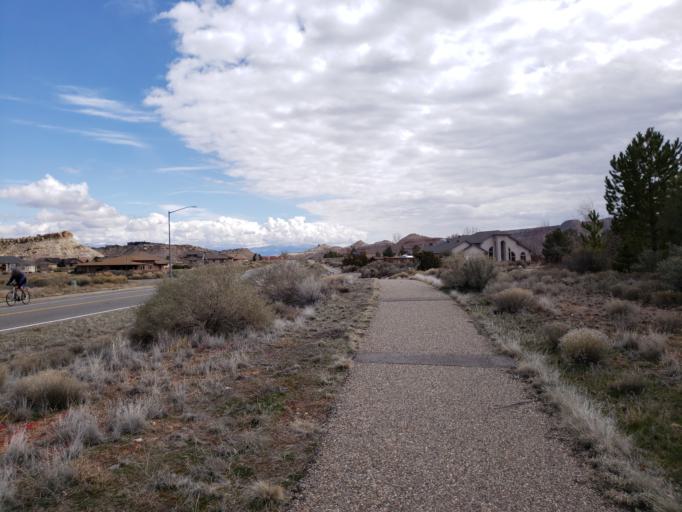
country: US
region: Colorado
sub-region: Mesa County
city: Redlands
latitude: 39.0535
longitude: -108.6422
